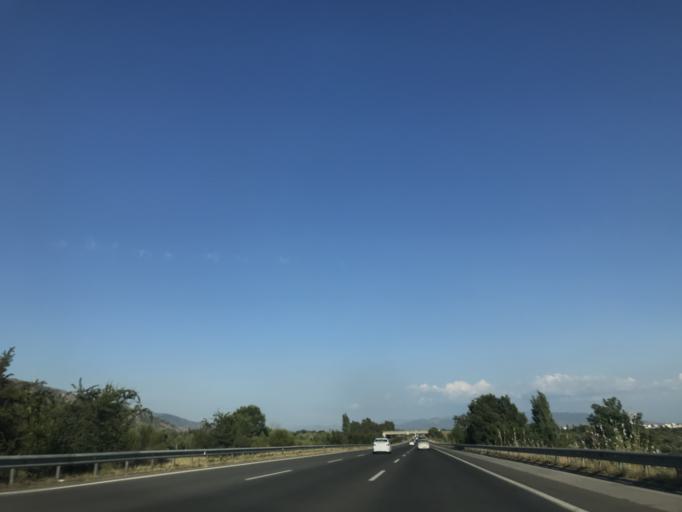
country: TR
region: Aydin
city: Incirliova
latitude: 37.8731
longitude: 27.7039
